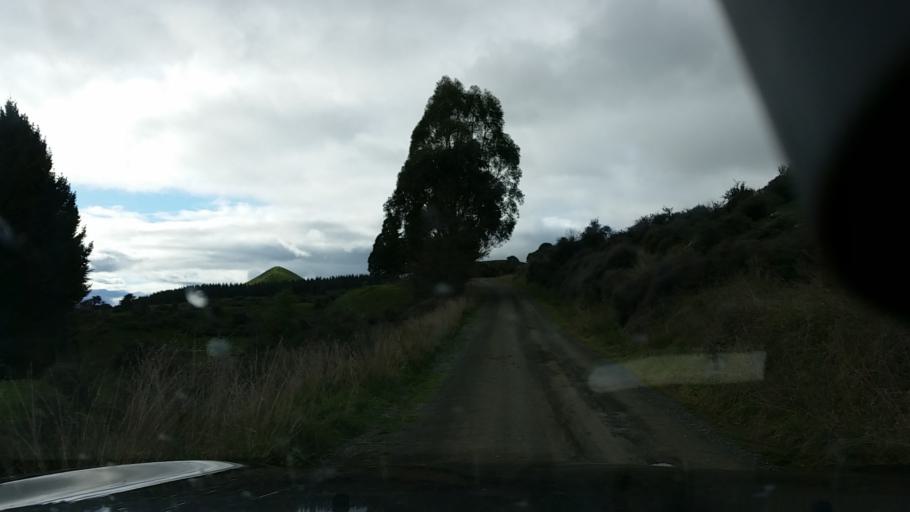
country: NZ
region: Marlborough
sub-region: Marlborough District
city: Blenheim
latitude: -41.6607
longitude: 173.6573
